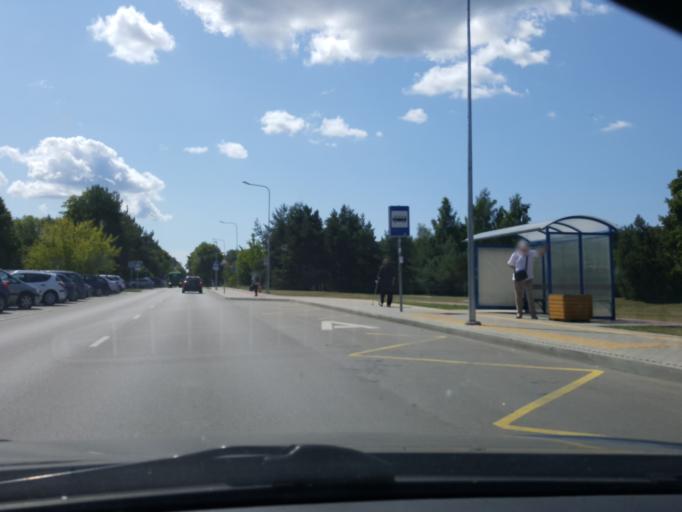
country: LT
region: Klaipedos apskritis
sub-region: Klaipeda
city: Palanga
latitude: 55.9356
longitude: 21.0777
